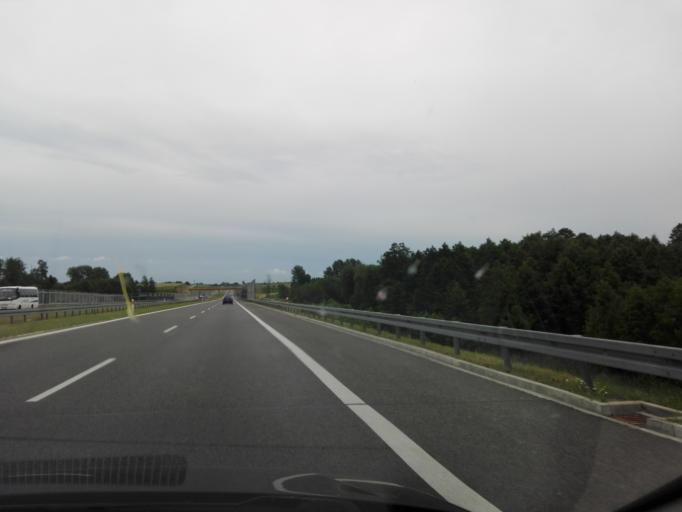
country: PL
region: Lublin Voivodeship
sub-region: Powiat lubelski
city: Jastkow
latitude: 51.3091
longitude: 22.3925
